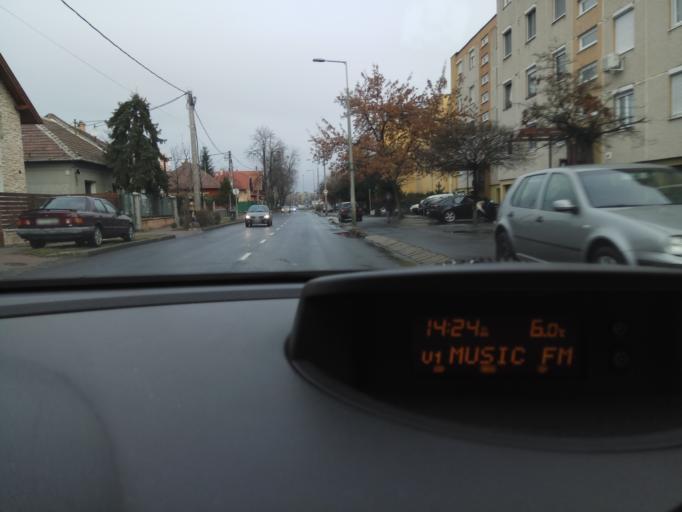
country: HU
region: Budapest
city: Budapest XV. keruelet
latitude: 47.5762
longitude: 19.1051
